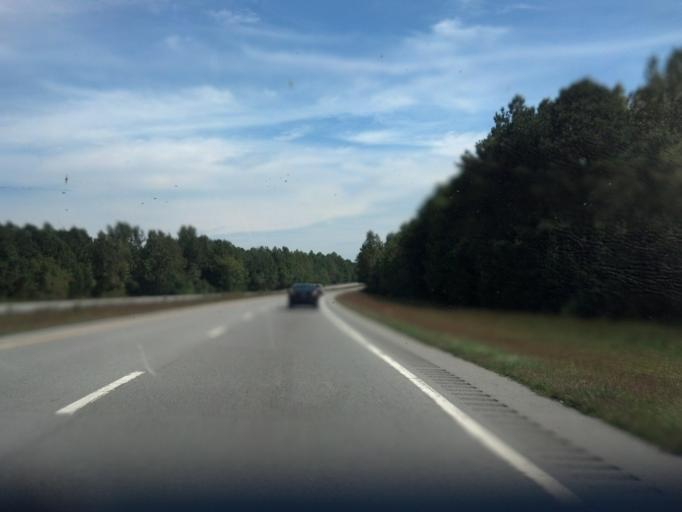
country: US
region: North Carolina
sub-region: Pitt County
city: Farmville
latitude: 35.6096
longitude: -77.5092
